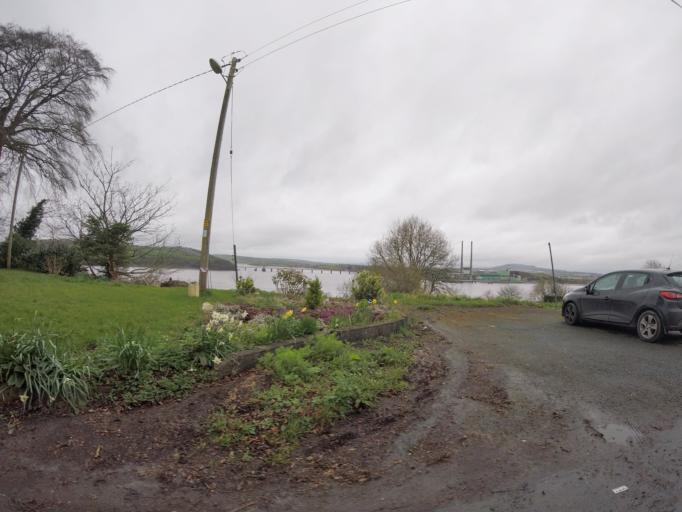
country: IE
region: Munster
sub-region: Waterford
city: Waterford
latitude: 52.2697
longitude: -6.9994
